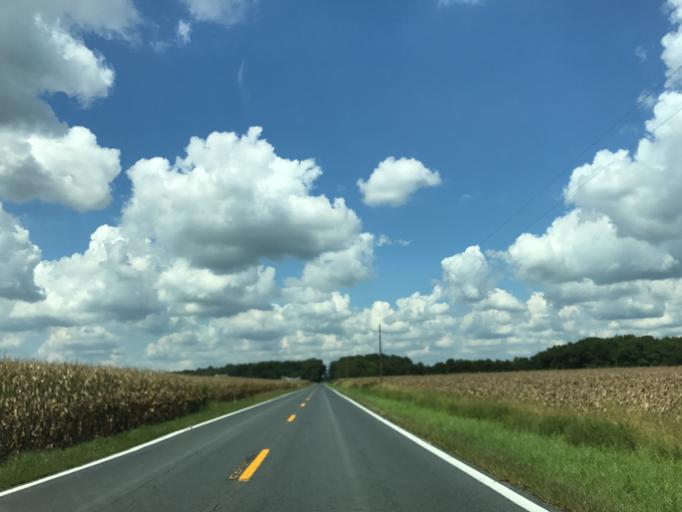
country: US
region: Maryland
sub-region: Caroline County
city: Ridgely
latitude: 39.0346
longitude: -75.9046
